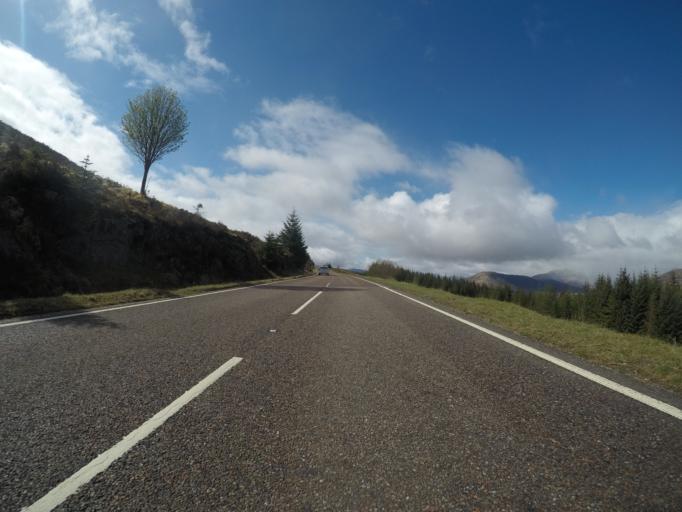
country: GB
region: Scotland
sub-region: Highland
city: Spean Bridge
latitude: 57.1011
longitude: -4.9920
